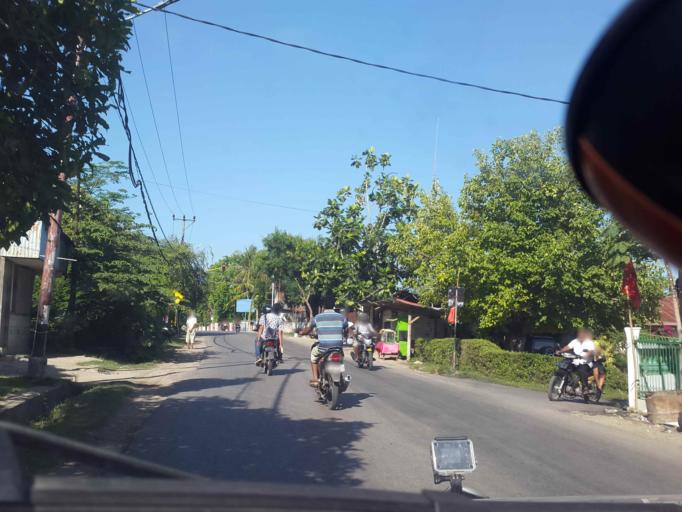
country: ID
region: East Nusa Tenggara
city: Airnona
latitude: -10.1796
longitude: 123.5902
